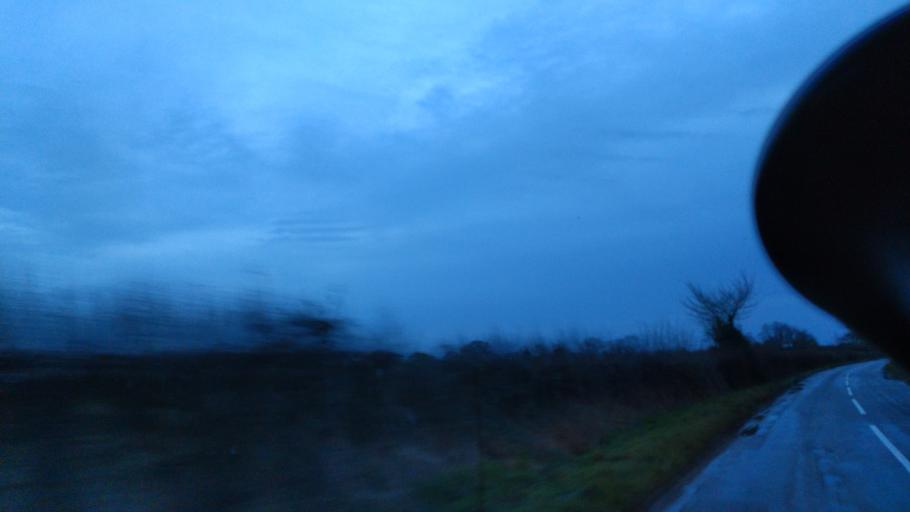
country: GB
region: England
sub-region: Oxfordshire
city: Shrivenham
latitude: 51.6086
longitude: -1.6704
